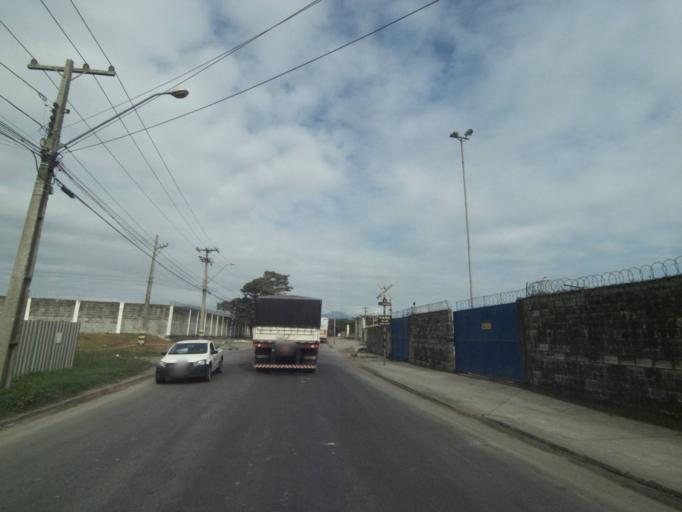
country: BR
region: Parana
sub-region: Paranagua
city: Paranagua
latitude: -25.5137
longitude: -48.5263
